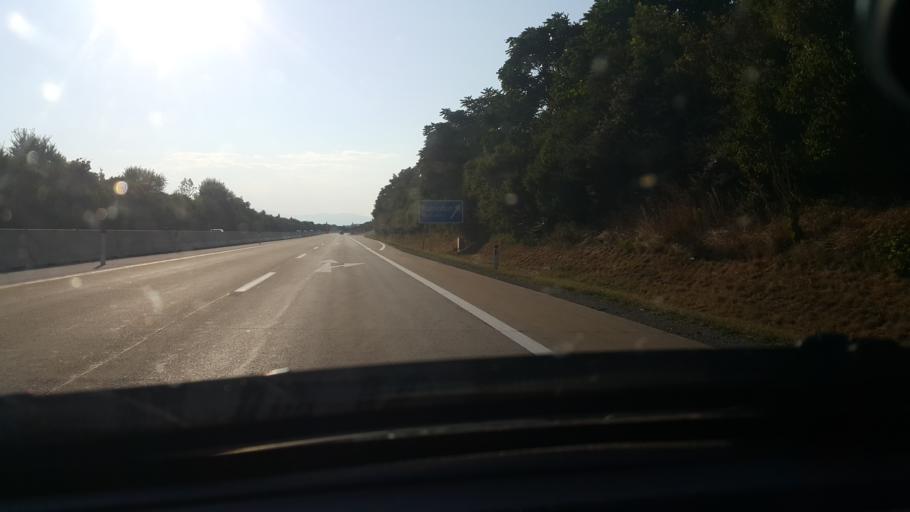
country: AT
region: Carinthia
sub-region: Politischer Bezirk Klagenfurt Land
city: Maria Saal
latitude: 46.6446
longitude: 14.3426
